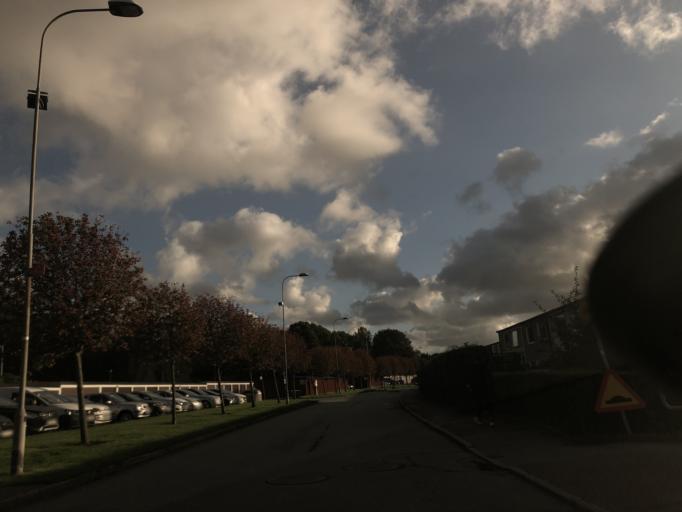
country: SE
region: Vaestra Goetaland
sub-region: Goteborg
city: Majorna
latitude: 57.7475
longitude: 11.9261
